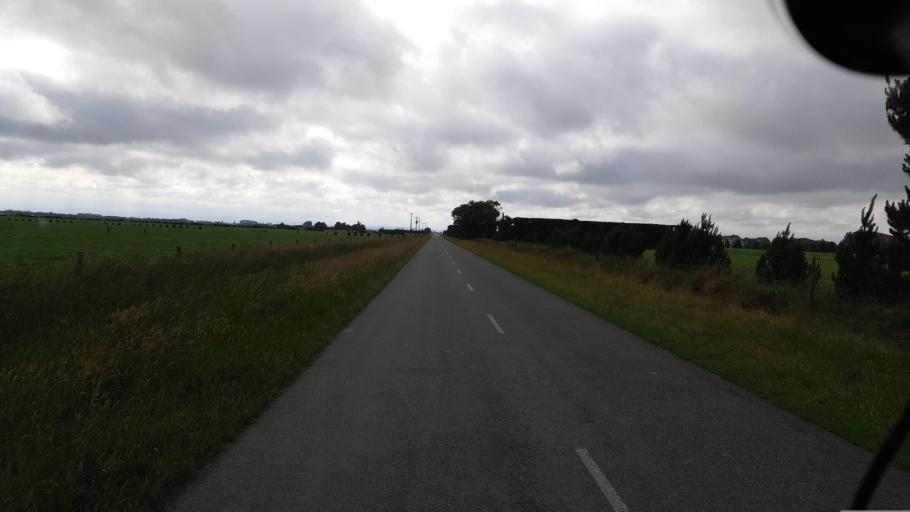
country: NZ
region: Canterbury
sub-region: Timaru District
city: Timaru
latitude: -44.2427
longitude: 171.3582
